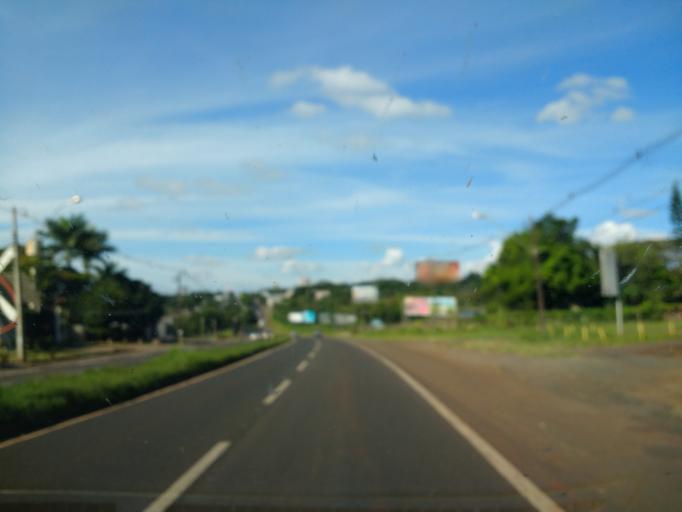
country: BR
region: Parana
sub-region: Maringa
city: Maringa
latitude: -23.4193
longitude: -51.9655
